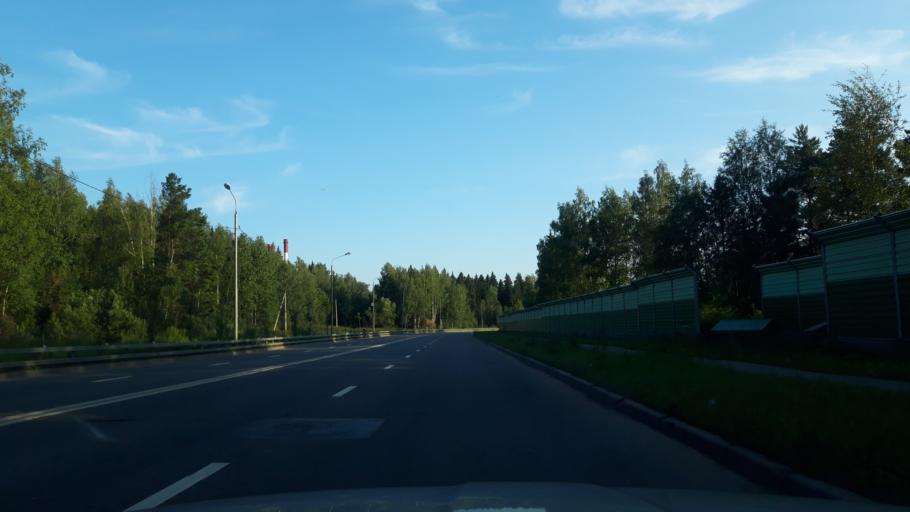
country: RU
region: Moskovskaya
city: Alabushevo
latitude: 56.0009
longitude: 37.1629
